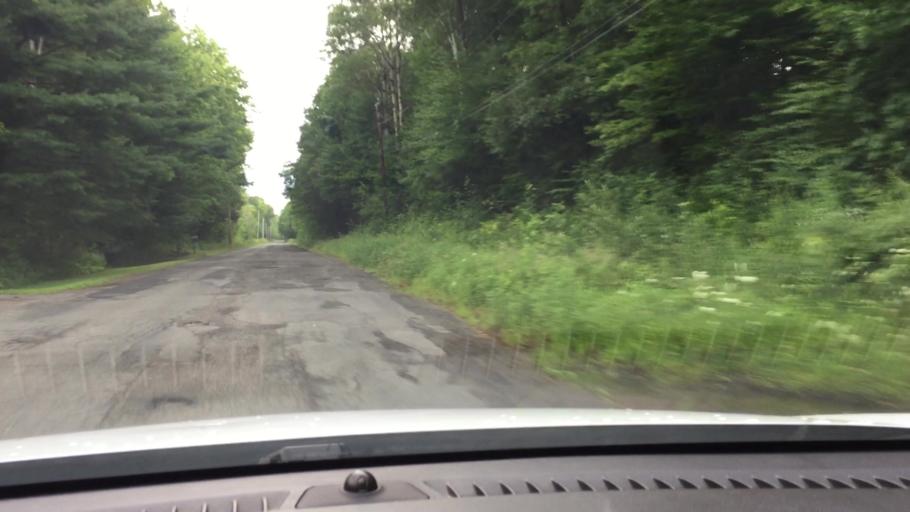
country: US
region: Massachusetts
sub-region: Hampshire County
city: Chesterfield
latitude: 42.2763
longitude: -72.9137
